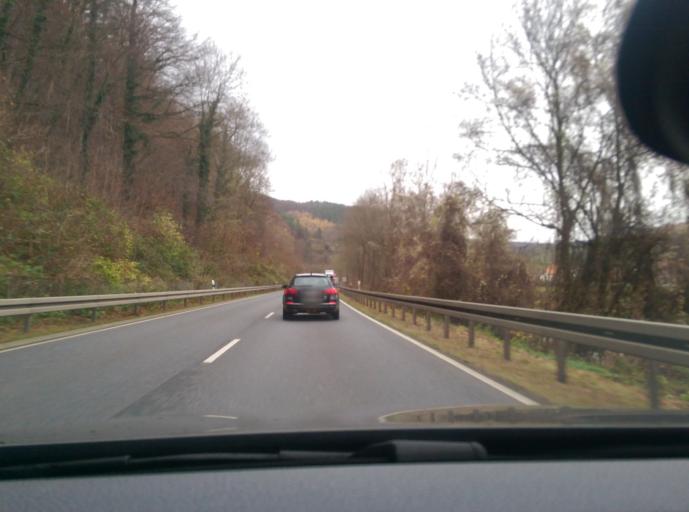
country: DE
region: Thuringia
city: Lindewerra
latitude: 51.3207
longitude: 9.9146
